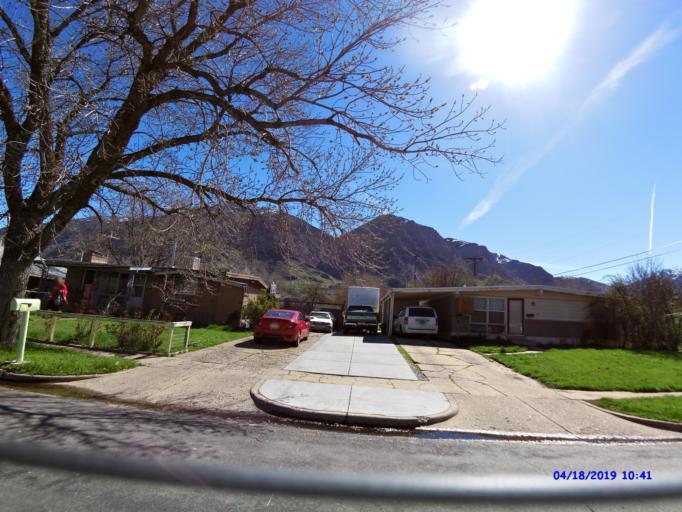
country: US
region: Utah
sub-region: Weber County
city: Harrisville
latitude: 41.2695
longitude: -111.9603
